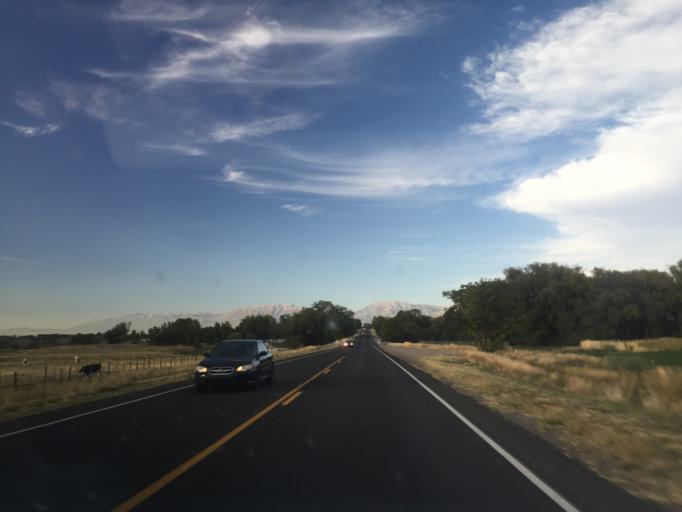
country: US
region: Utah
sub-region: Utah County
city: Santaquin
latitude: 40.0004
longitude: -111.7509
